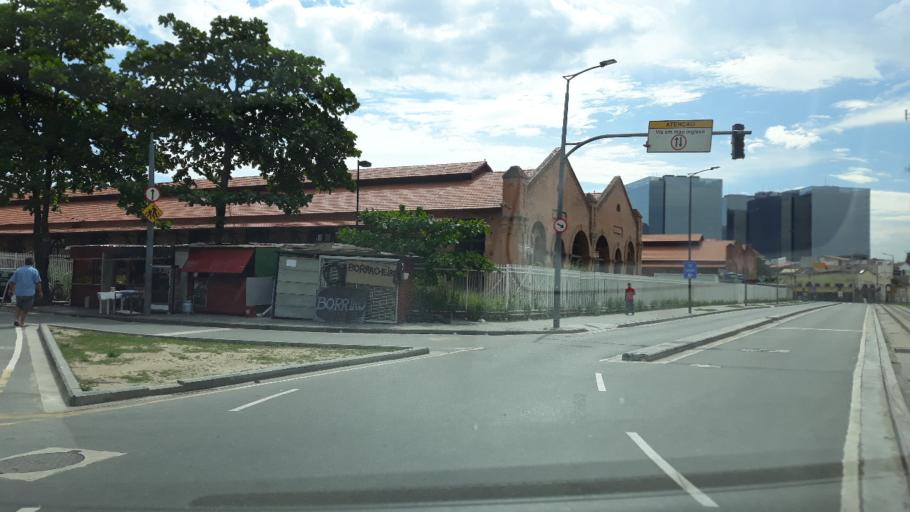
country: BR
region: Rio de Janeiro
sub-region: Rio De Janeiro
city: Rio de Janeiro
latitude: -22.8978
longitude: -43.1975
